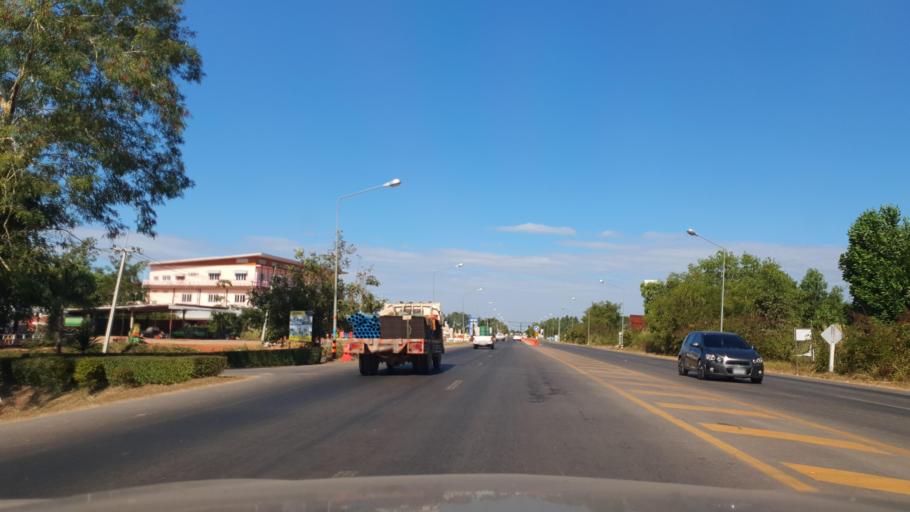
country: TH
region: Nakhon Phanom
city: Ban Phaeng
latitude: 17.9584
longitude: 104.2119
